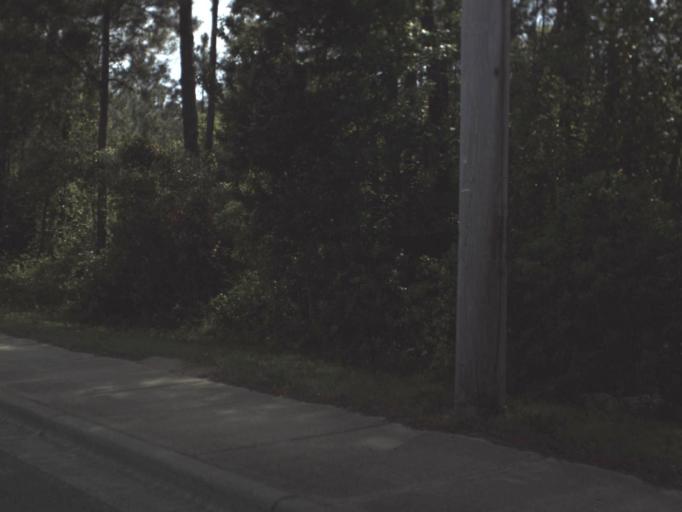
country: US
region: Florida
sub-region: Santa Rosa County
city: Navarre
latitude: 30.4294
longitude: -86.8667
